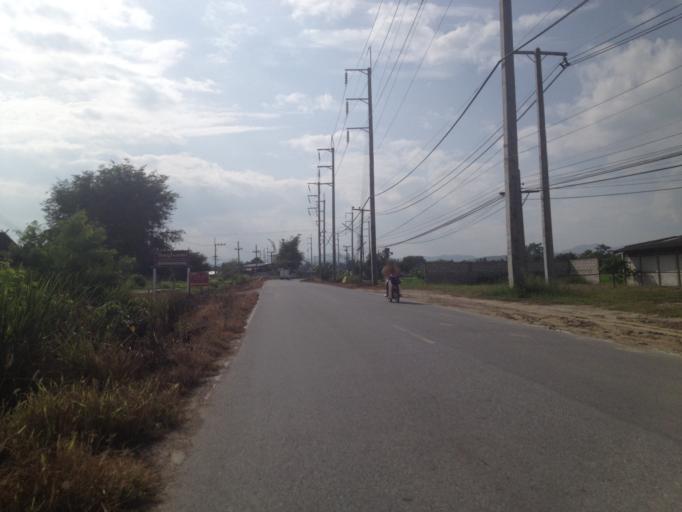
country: TH
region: Chiang Mai
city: Hang Dong
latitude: 18.6755
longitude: 98.9085
